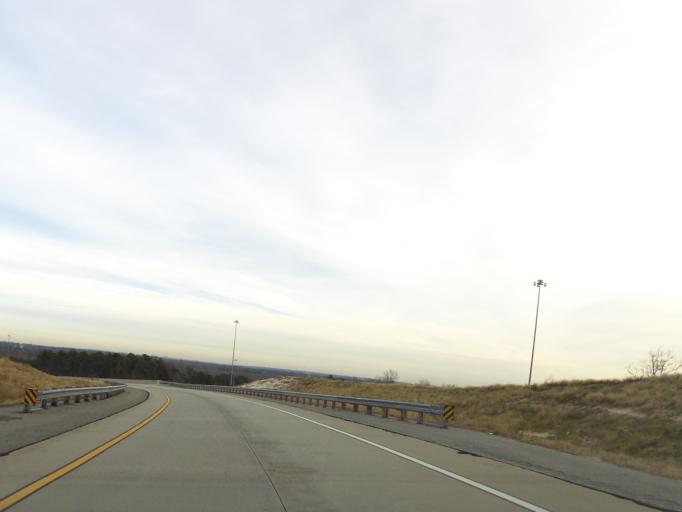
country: US
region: Georgia
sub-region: Bibb County
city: West Point
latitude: 32.7553
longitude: -83.7085
